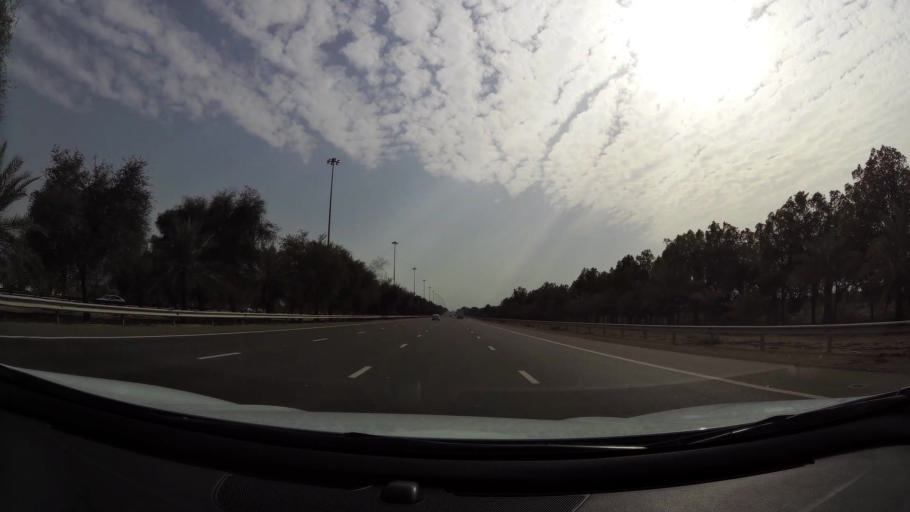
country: AE
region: Abu Dhabi
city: Abu Dhabi
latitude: 24.5116
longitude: 54.6863
